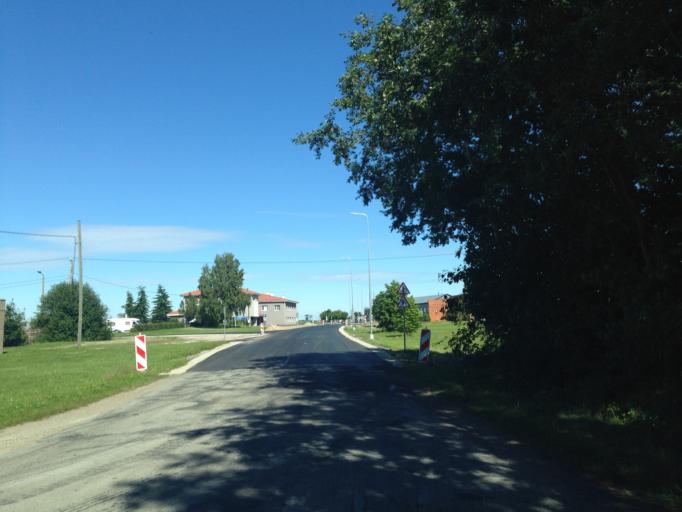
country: EE
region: Harju
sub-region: Kuusalu vald
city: Kuusalu
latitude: 59.4518
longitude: 25.3790
